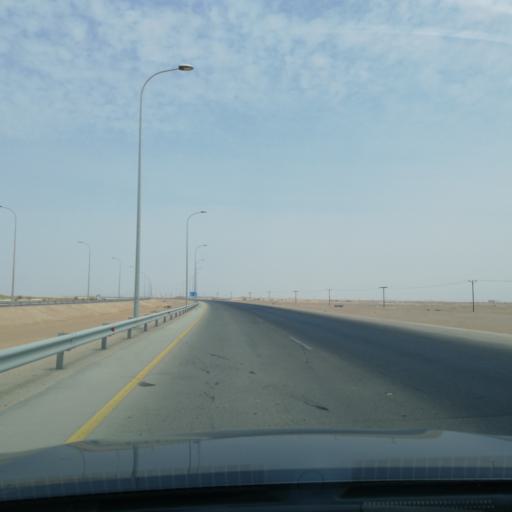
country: OM
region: Zufar
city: Salalah
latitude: 17.6914
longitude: 54.0517
